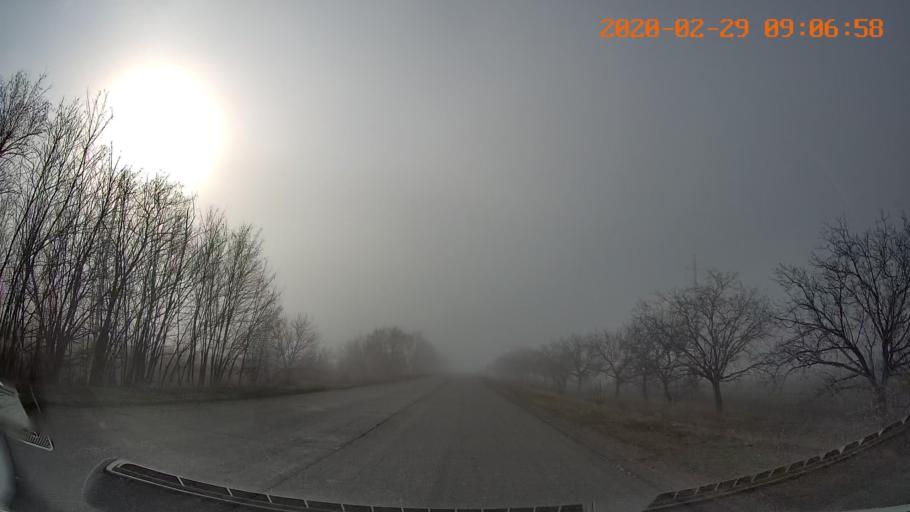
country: MD
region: Telenesti
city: Tiraspolul Nou
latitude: 46.8685
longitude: 29.7469
